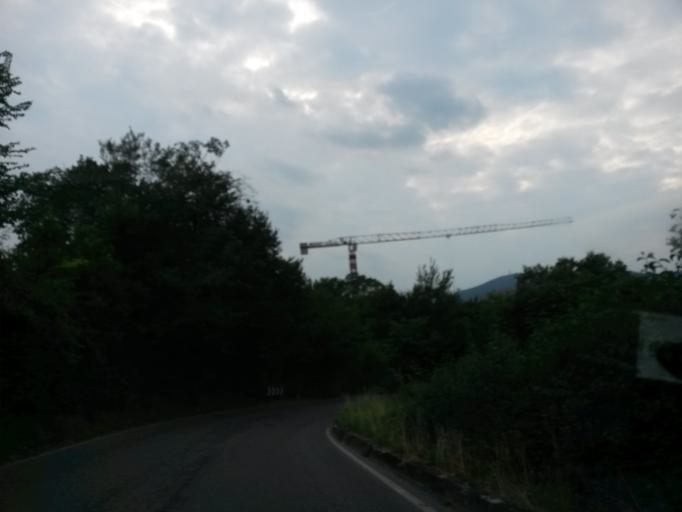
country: IT
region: Lombardy
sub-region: Provincia di Brescia
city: Cunettone-Villa
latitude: 45.5940
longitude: 10.5194
